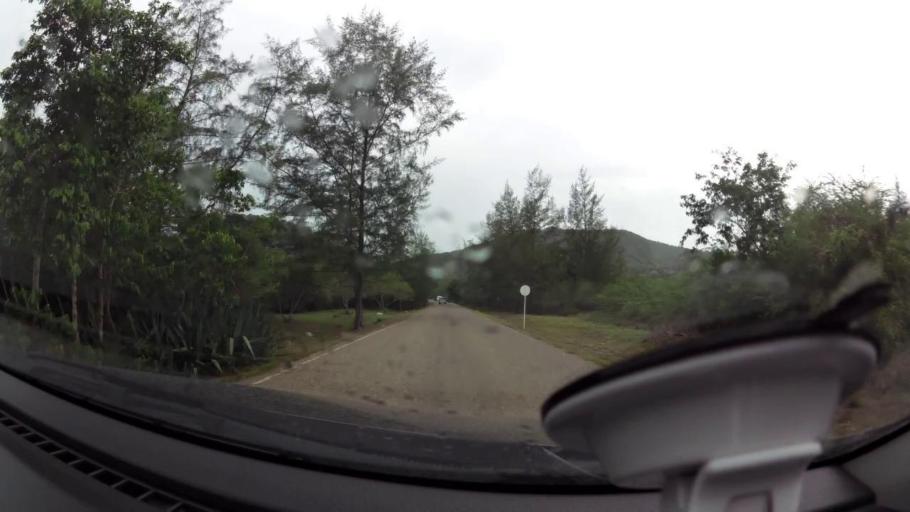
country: TH
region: Prachuap Khiri Khan
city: Pran Buri
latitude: 12.4192
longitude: 99.9832
